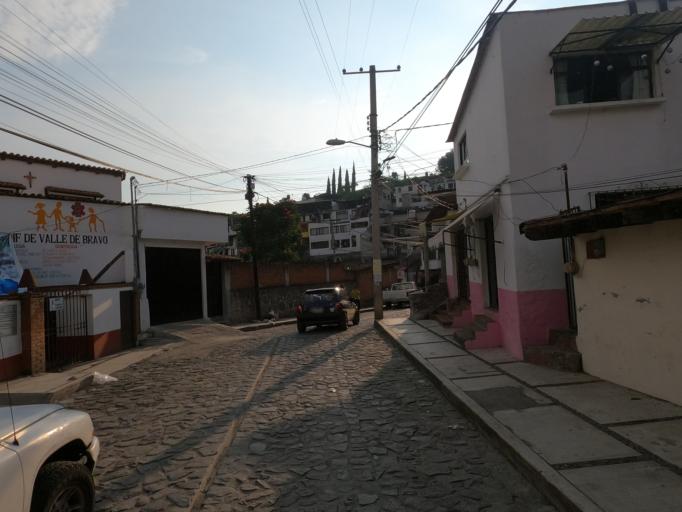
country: MX
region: Mexico
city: Valle de Bravo
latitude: 19.2016
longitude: -100.1284
